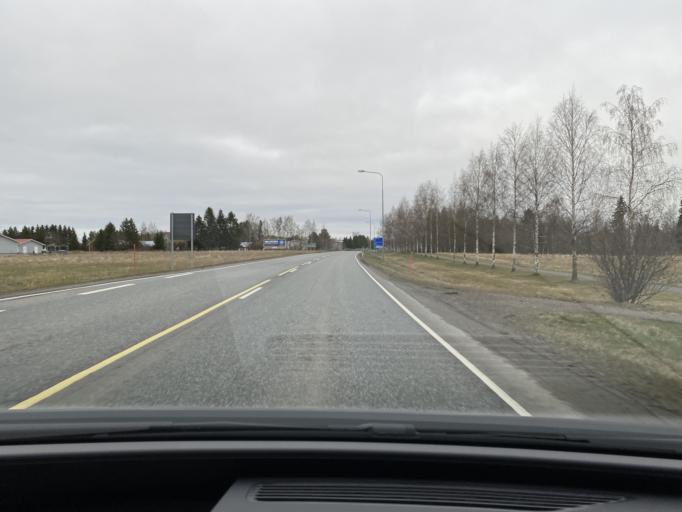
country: FI
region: Satakunta
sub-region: Pori
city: Huittinen
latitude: 61.1847
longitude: 22.6850
